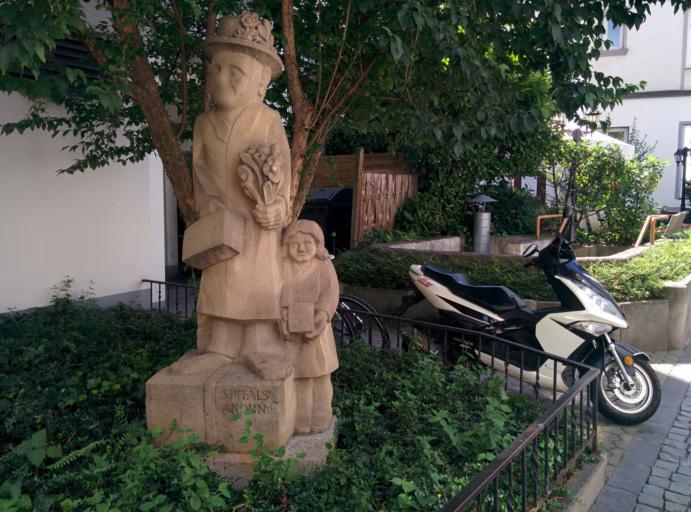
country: DE
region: Rheinland-Pfalz
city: Koblenz
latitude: 50.3613
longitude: 7.5958
